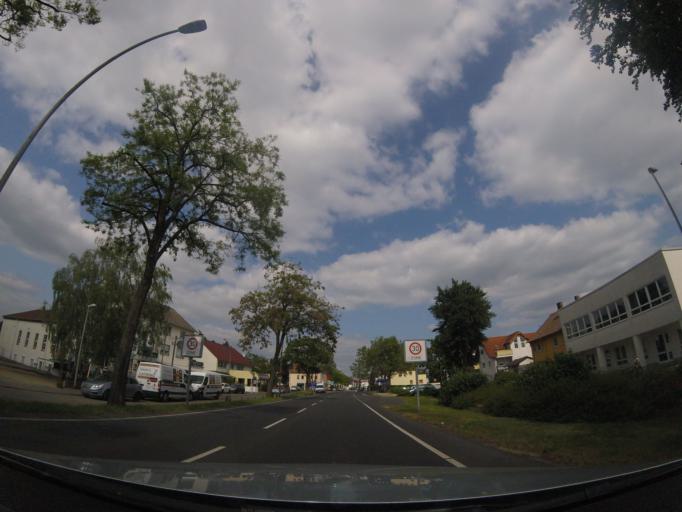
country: DE
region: Hesse
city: Raunheim
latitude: 50.0123
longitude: 8.4455
